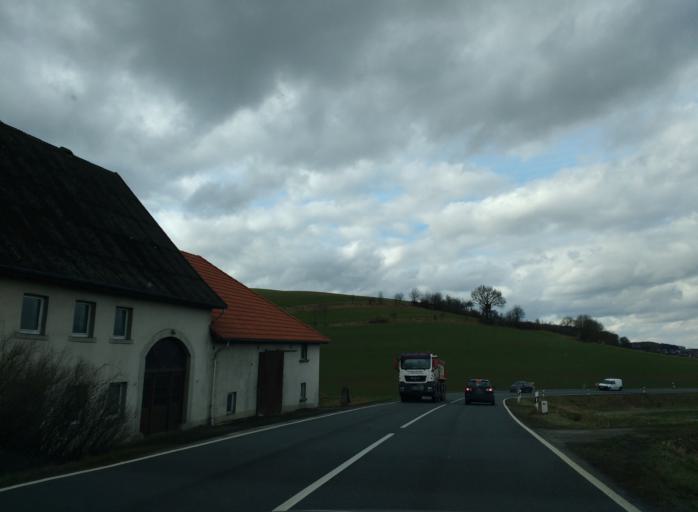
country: DE
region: North Rhine-Westphalia
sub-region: Regierungsbezirk Detmold
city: Lemgo
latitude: 52.0880
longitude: 8.9340
